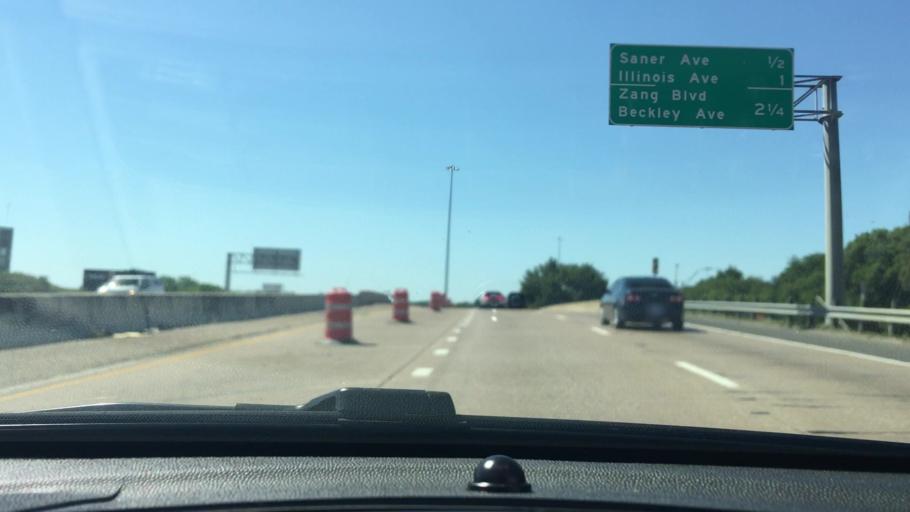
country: US
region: Texas
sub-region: Dallas County
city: Cockrell Hill
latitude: 32.7051
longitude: -96.8268
